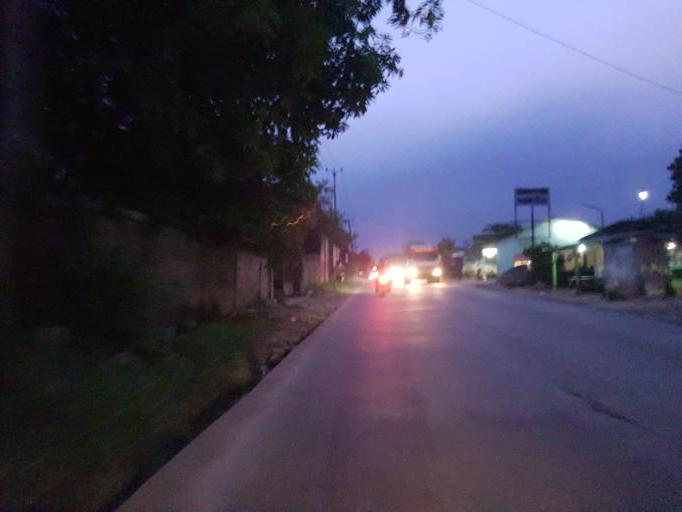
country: ID
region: West Java
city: Serpong
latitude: -6.3114
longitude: 106.6568
